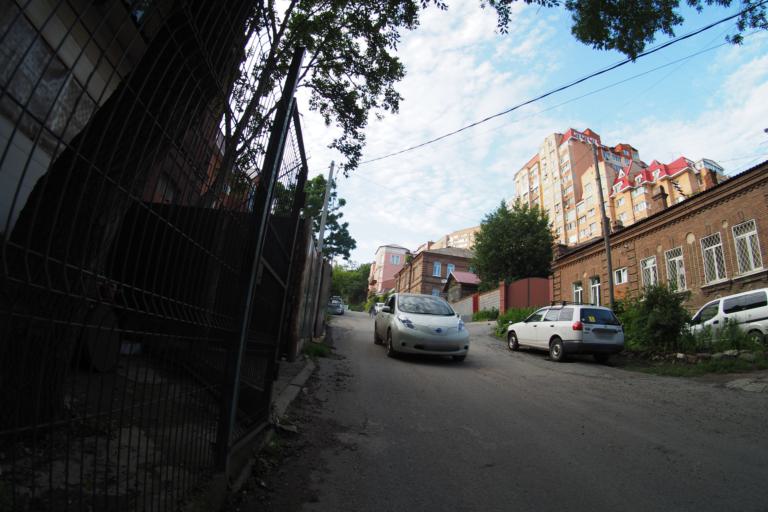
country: RU
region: Primorskiy
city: Vladivostok
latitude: 43.1128
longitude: 131.9213
